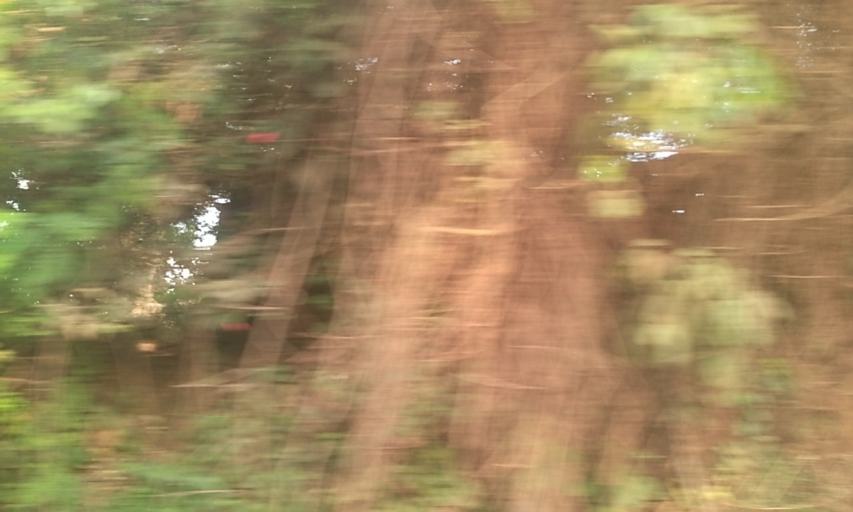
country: UG
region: Central Region
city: Kampala Central Division
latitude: 0.3079
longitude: 32.5533
